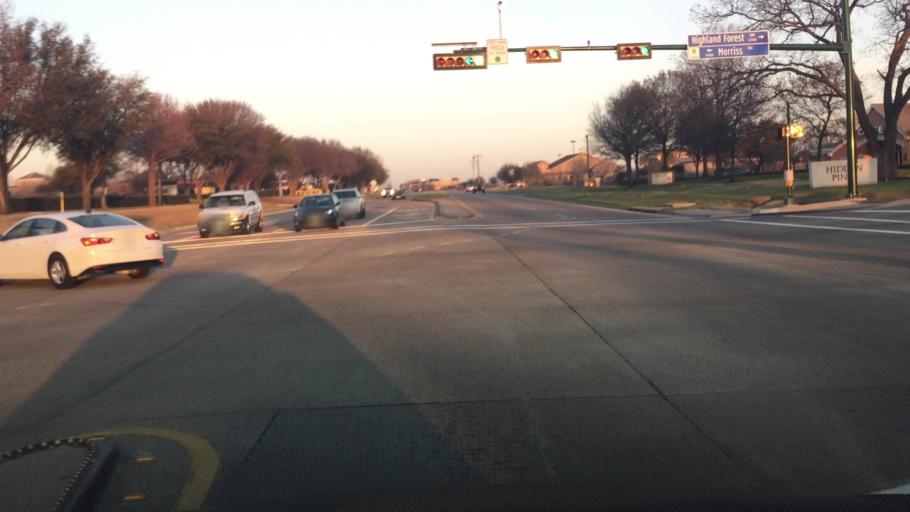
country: US
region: Texas
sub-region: Denton County
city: Highland Village
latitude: 33.0725
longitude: -97.0617
